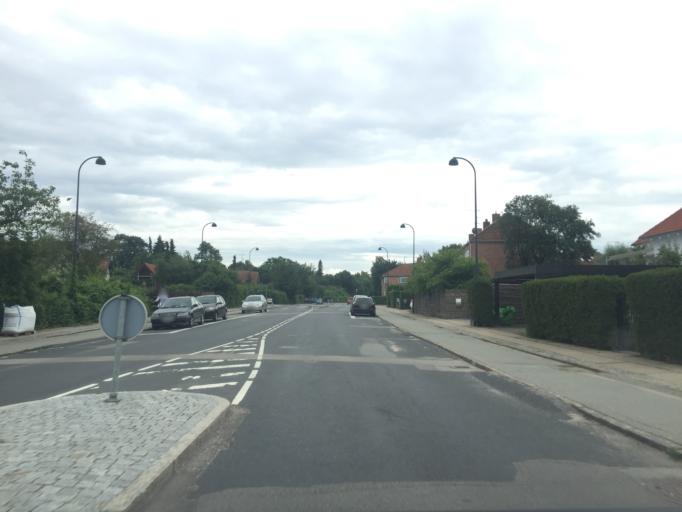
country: DK
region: Capital Region
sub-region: Lyngby-Tarbaek Kommune
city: Kongens Lyngby
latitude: 55.7601
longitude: 12.5364
